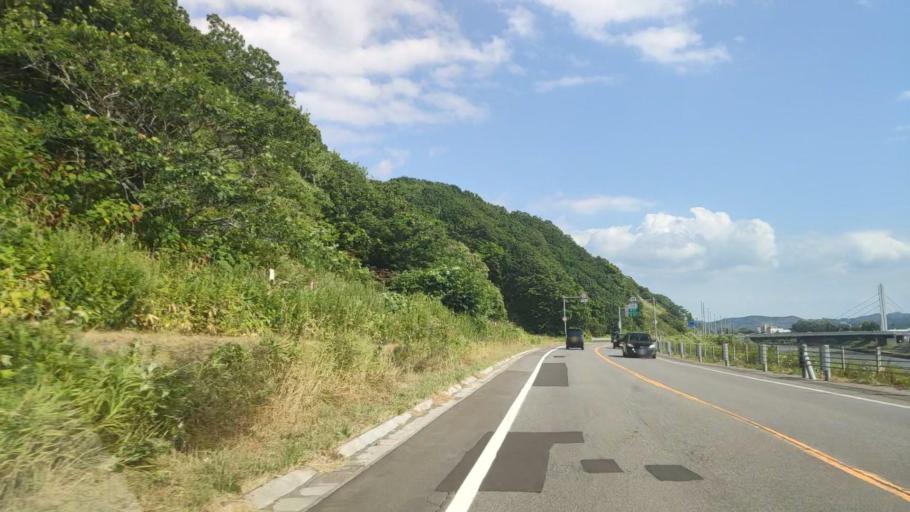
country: JP
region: Hokkaido
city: Rumoi
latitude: 43.9505
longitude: 141.6469
